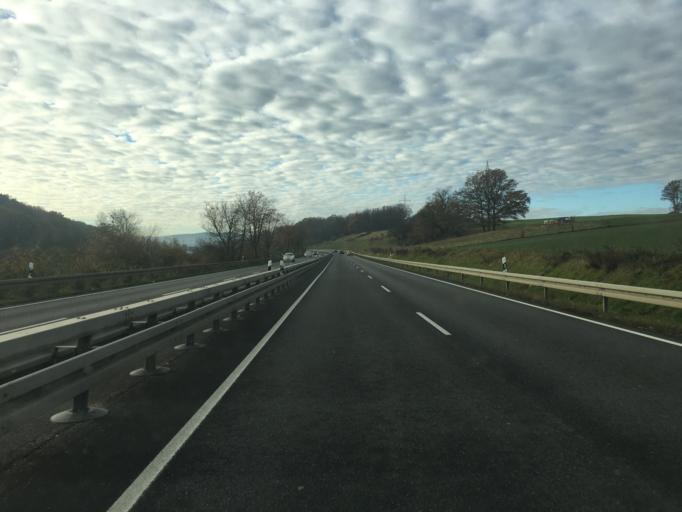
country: DE
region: North Rhine-Westphalia
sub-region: Regierungsbezirk Koln
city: Mechernich
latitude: 50.6267
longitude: 6.6708
